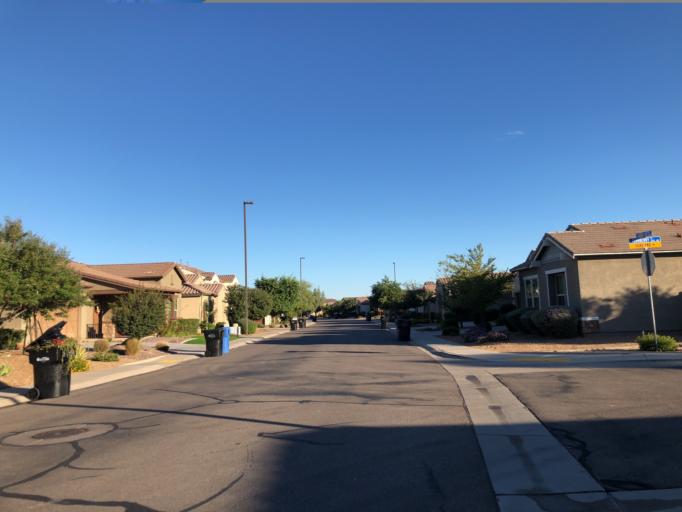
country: US
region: Arizona
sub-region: Maricopa County
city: Queen Creek
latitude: 33.2259
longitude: -111.7086
